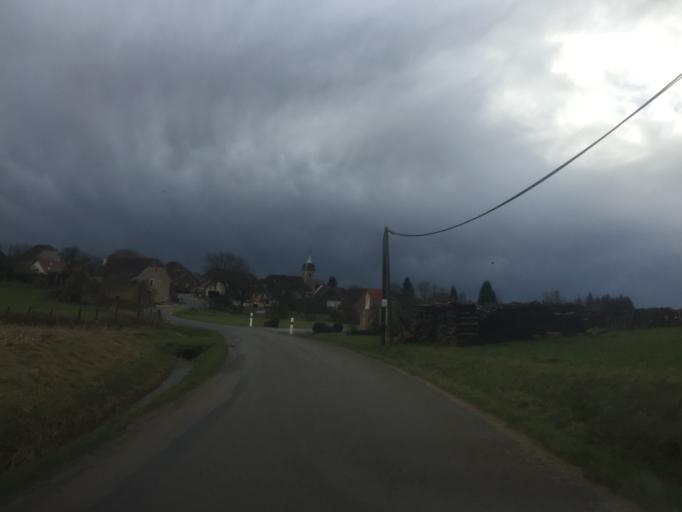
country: FR
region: Franche-Comte
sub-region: Departement du Jura
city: Dampierre
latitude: 47.1988
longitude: 5.7160
